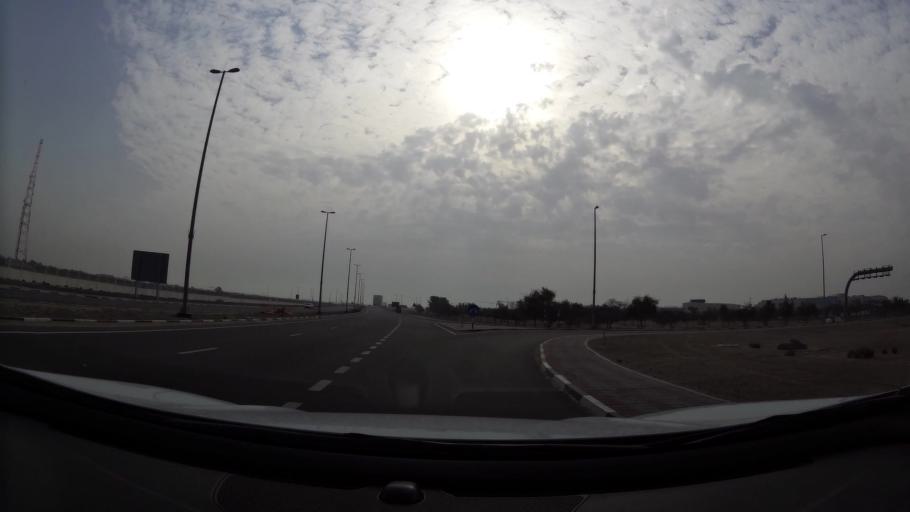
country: AE
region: Abu Dhabi
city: Abu Dhabi
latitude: 24.6843
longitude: 54.7758
